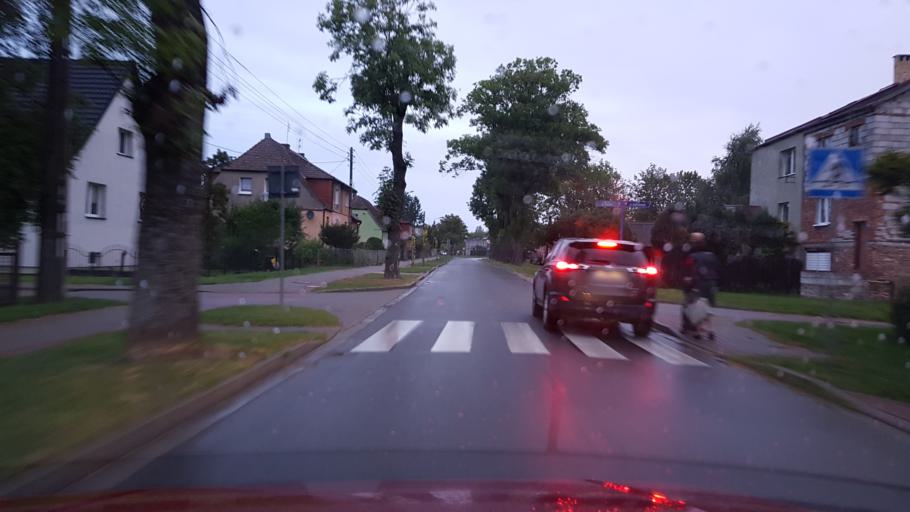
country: PL
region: West Pomeranian Voivodeship
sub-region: Powiat slawienski
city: Slawno
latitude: 54.3477
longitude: 16.6811
